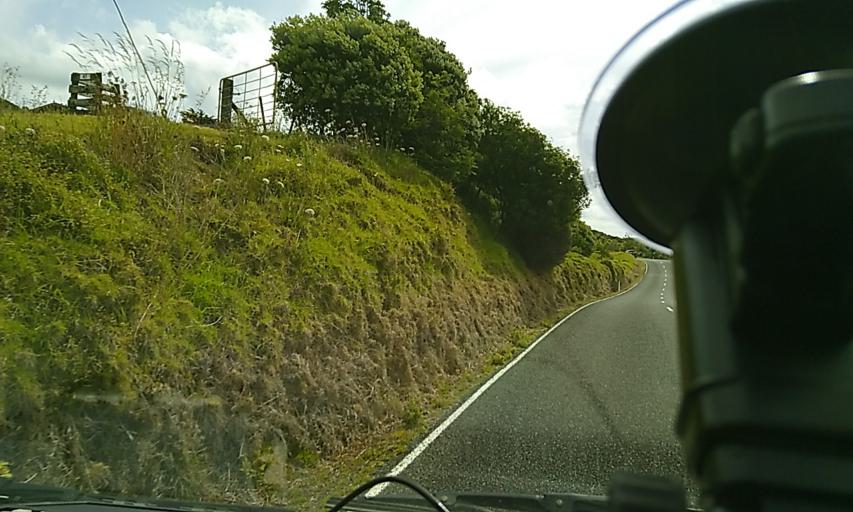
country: NZ
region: Northland
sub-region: Far North District
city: Ahipara
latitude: -35.5379
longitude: 173.3780
